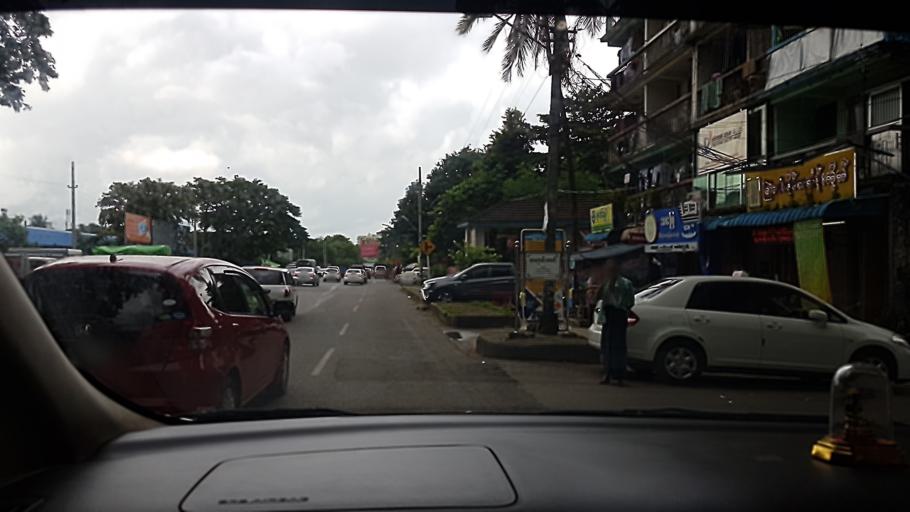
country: MM
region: Yangon
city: Yangon
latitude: 16.8071
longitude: 96.1257
